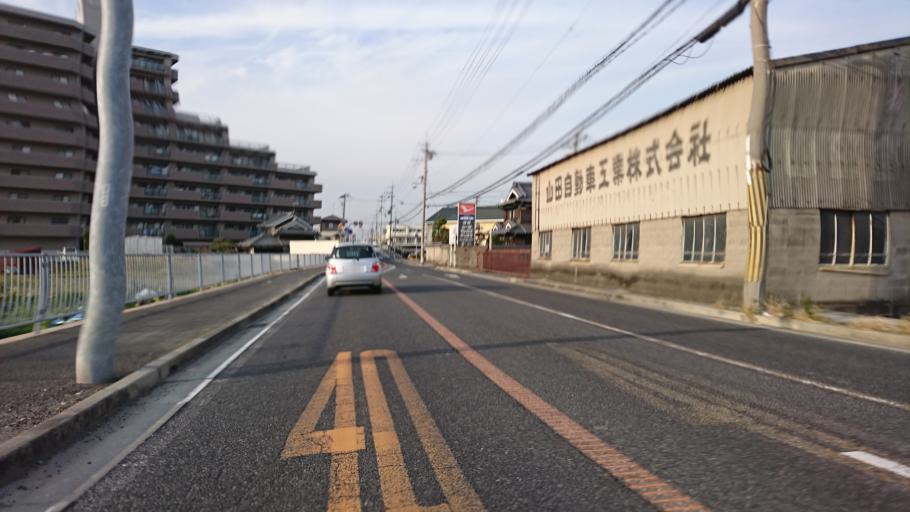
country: JP
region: Hyogo
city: Kakogawacho-honmachi
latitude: 34.7132
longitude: 134.8624
